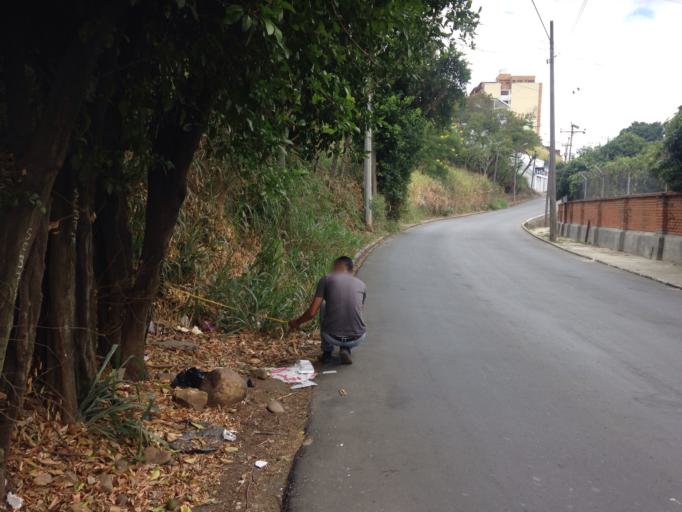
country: CO
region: Valle del Cauca
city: Cali
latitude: 3.4709
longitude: -76.5318
